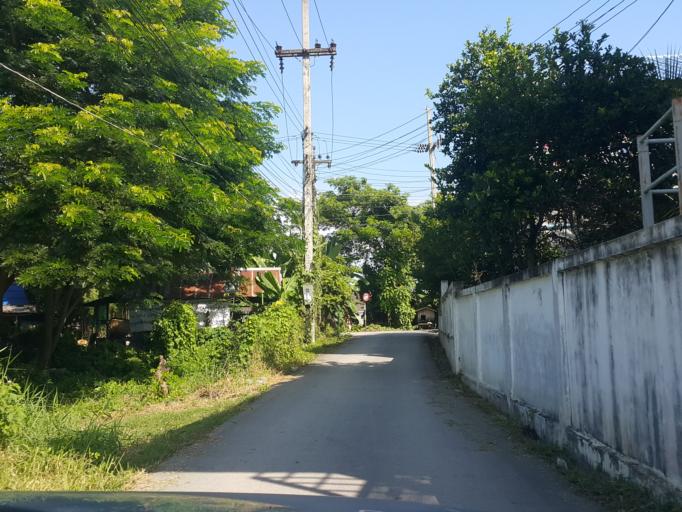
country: TH
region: Chiang Mai
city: Saraphi
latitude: 18.7334
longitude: 99.0458
